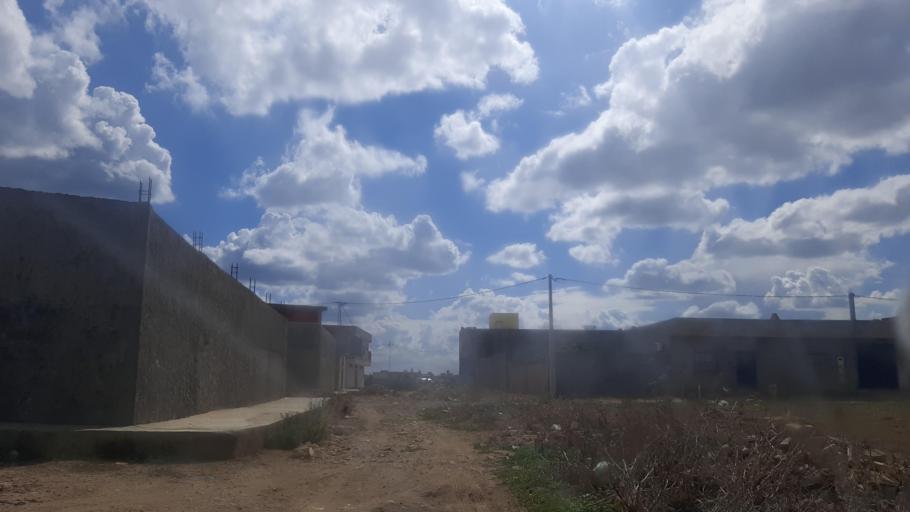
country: TN
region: Nabul
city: Korba
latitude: 36.5937
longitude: 10.8566
